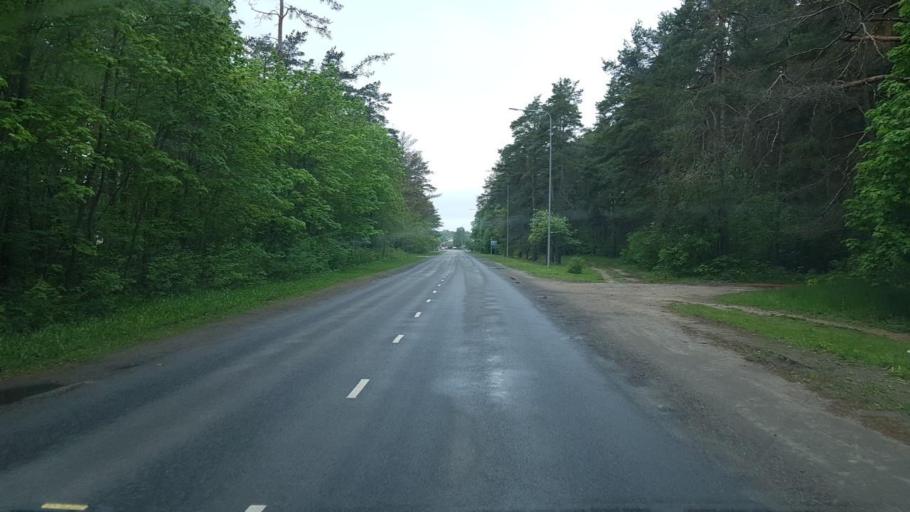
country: EE
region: Laeaene
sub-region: Haapsalu linn
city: Haapsalu
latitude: 58.9283
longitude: 23.5376
